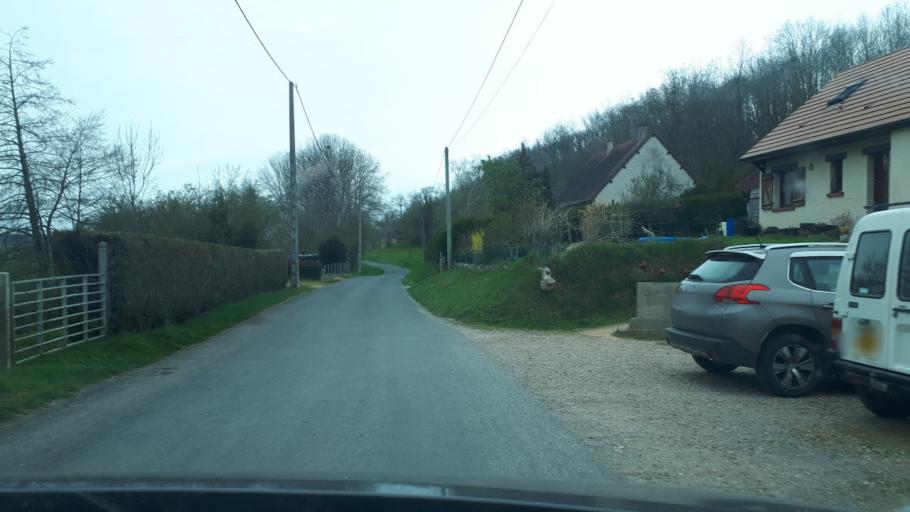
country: FR
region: Centre
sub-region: Departement du Loir-et-Cher
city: Lunay
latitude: 47.7653
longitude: 0.9212
